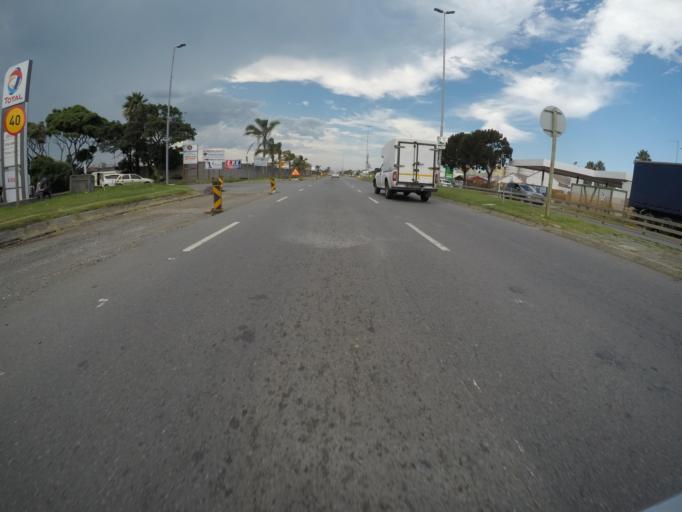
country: ZA
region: Eastern Cape
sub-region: Buffalo City Metropolitan Municipality
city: East London
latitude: -33.0319
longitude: 27.8844
